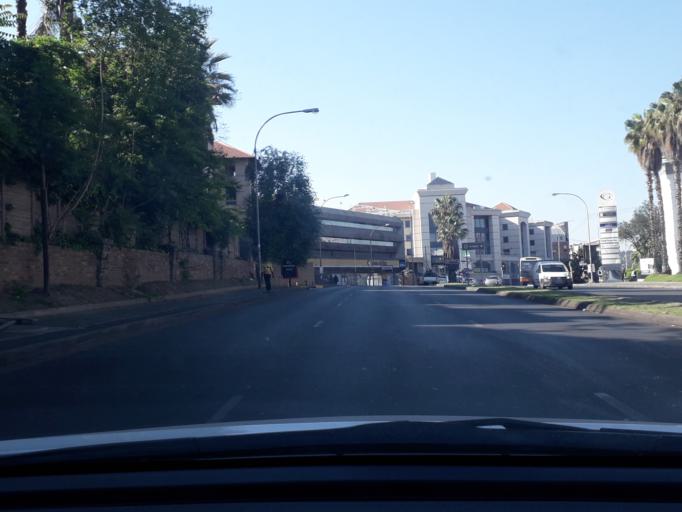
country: ZA
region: Gauteng
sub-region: City of Johannesburg Metropolitan Municipality
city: Johannesburg
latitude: -26.1442
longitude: 28.0360
